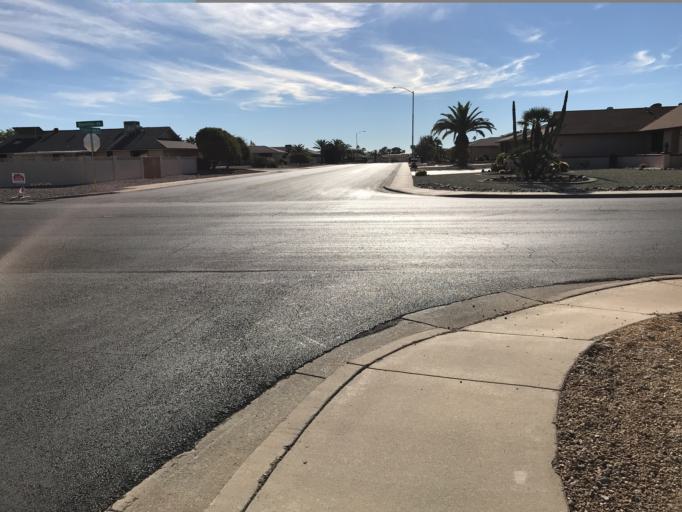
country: US
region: Arizona
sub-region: Maricopa County
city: Sun City West
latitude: 33.6673
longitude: -112.3277
